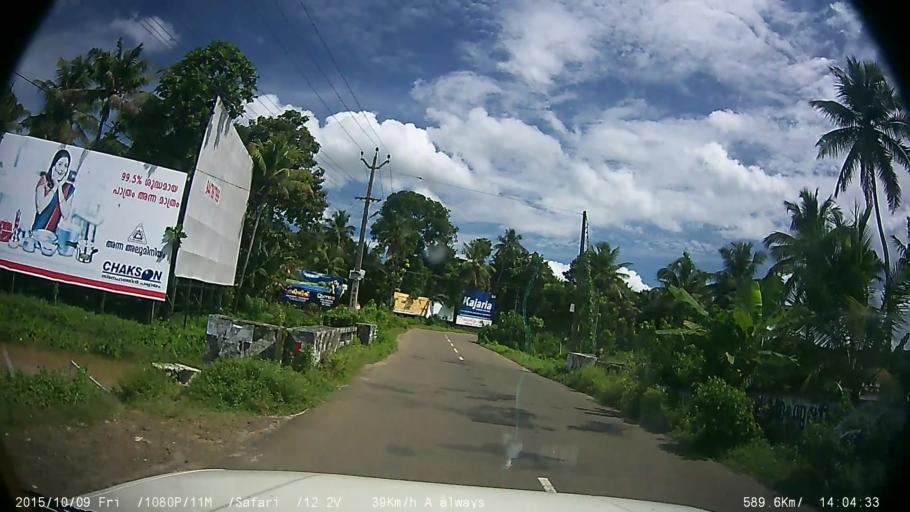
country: IN
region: Kerala
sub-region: Ernakulam
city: Piravam
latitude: 9.8884
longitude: 76.5635
